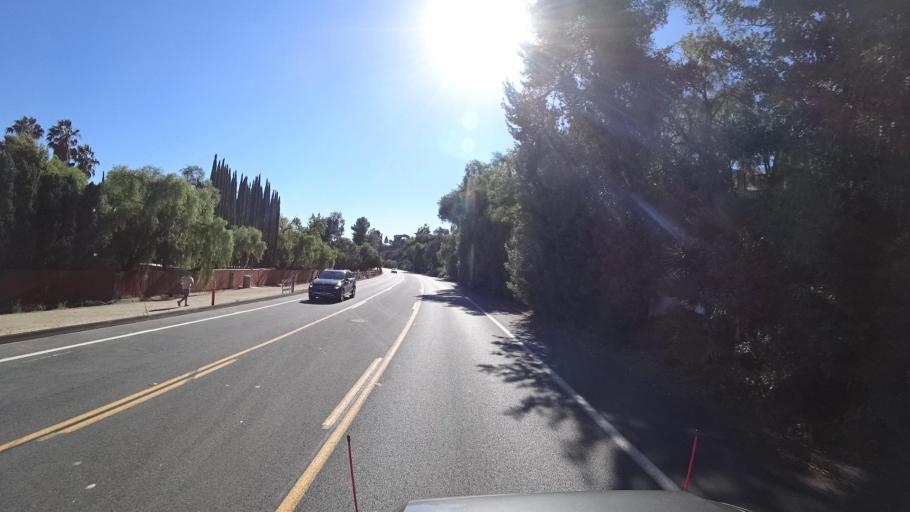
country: US
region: California
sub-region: San Diego County
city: Bonita
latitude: 32.6646
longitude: -117.0408
